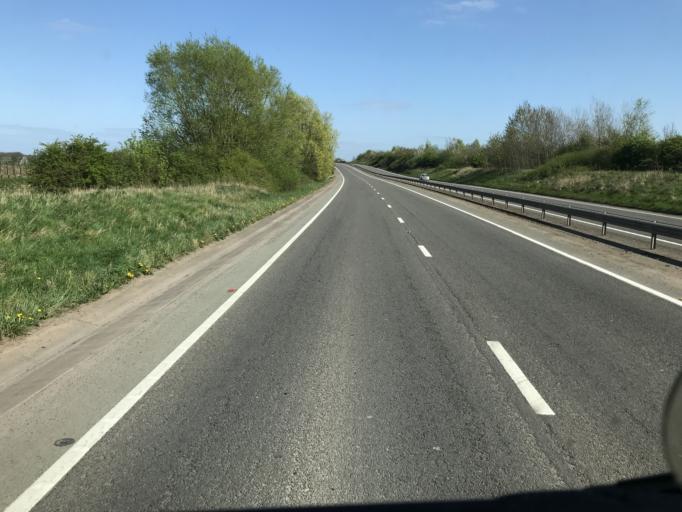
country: GB
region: England
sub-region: Cheshire East
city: Crewe
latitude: 53.0703
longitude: -2.4314
